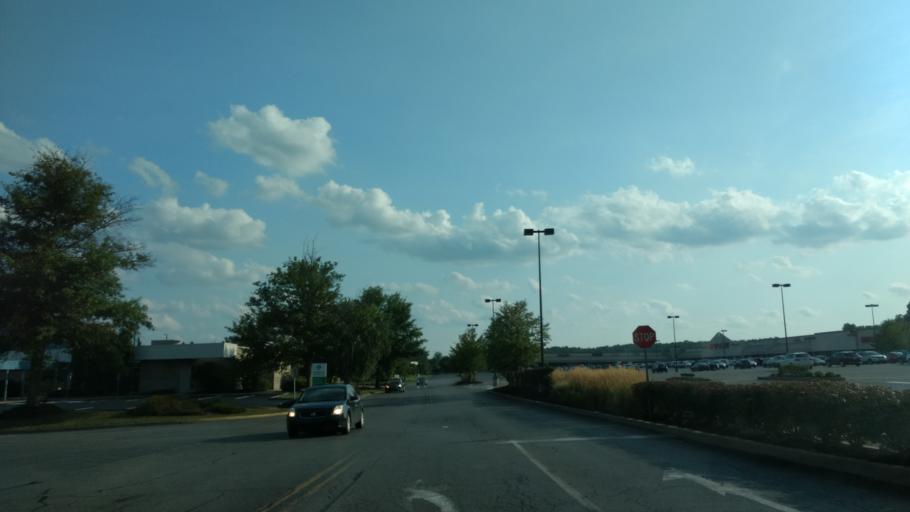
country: US
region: Pennsylvania
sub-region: Allegheny County
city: Gibsonia
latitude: 40.6208
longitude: -79.9453
